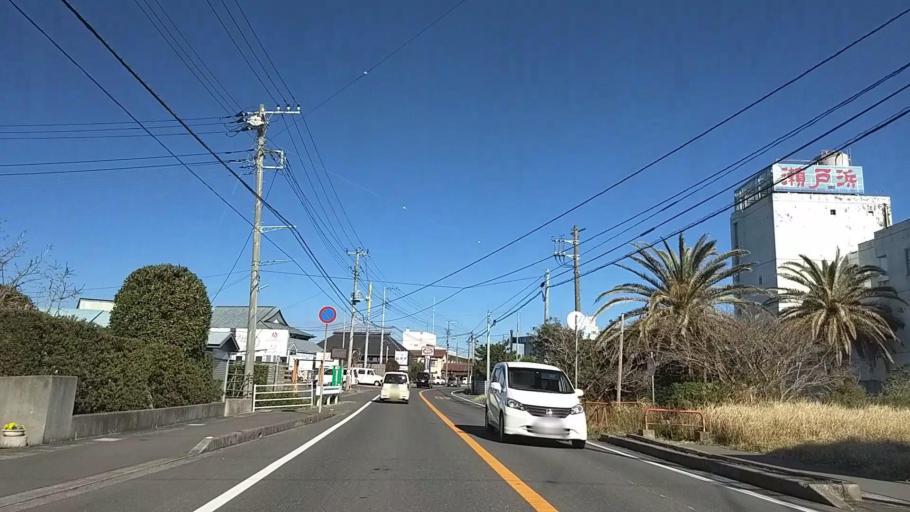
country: JP
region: Chiba
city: Tateyama
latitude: 34.9743
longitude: 139.9626
